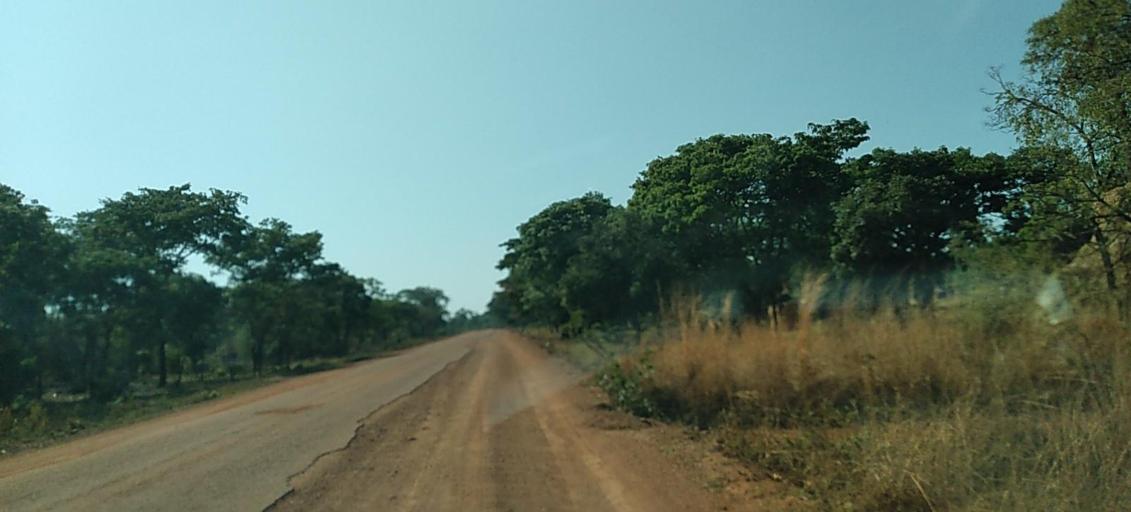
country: ZM
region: North-Western
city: Mwinilunga
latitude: -11.8973
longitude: 25.2738
